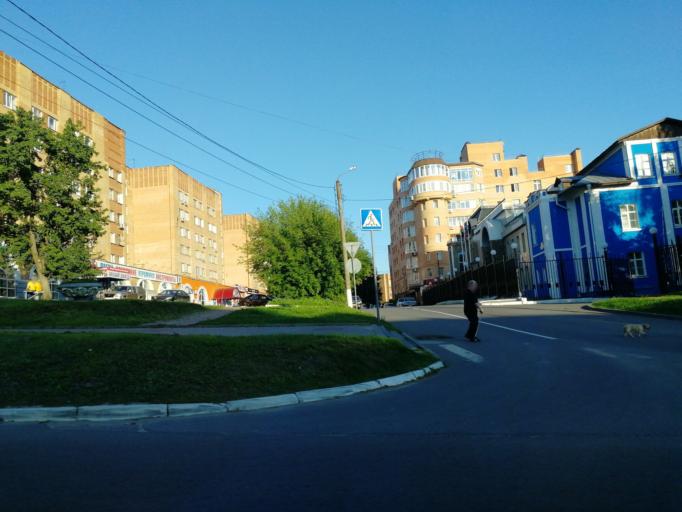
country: RU
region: Kaluga
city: Kaluga
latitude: 54.5119
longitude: 36.2362
